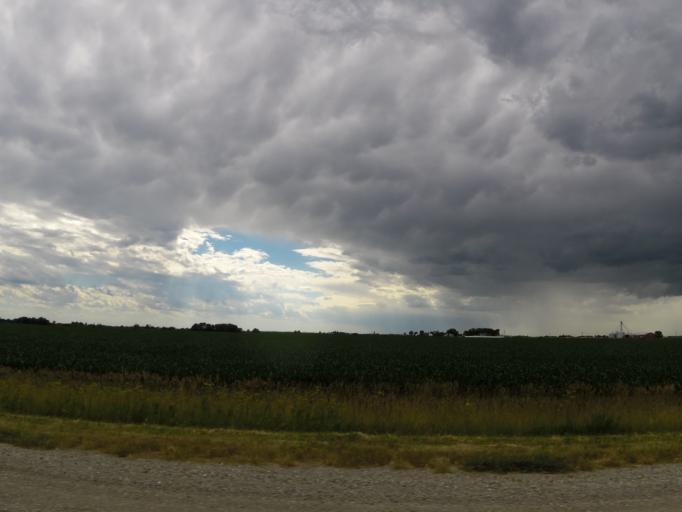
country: US
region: Iowa
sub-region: Henry County
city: Winfield
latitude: 41.0883
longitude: -91.5450
